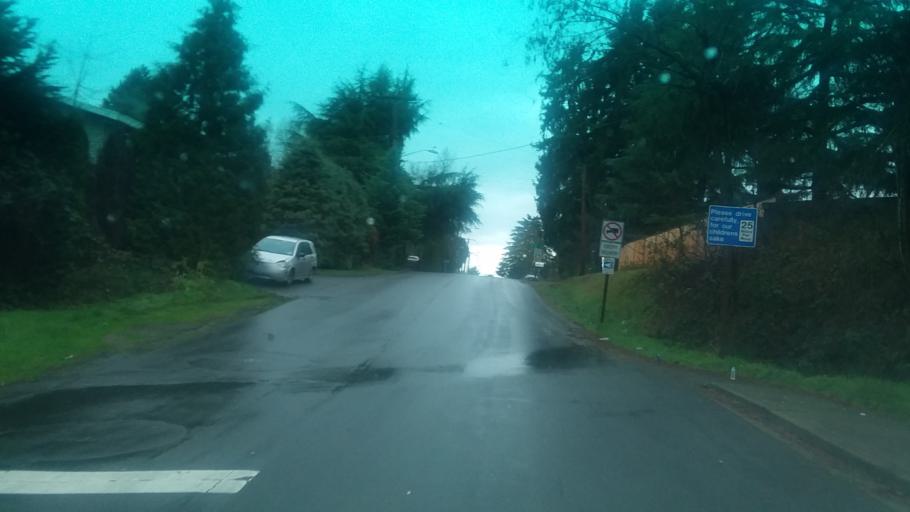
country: US
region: Washington
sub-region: King County
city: East Hill-Meridian
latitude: 47.4159
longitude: -122.2126
